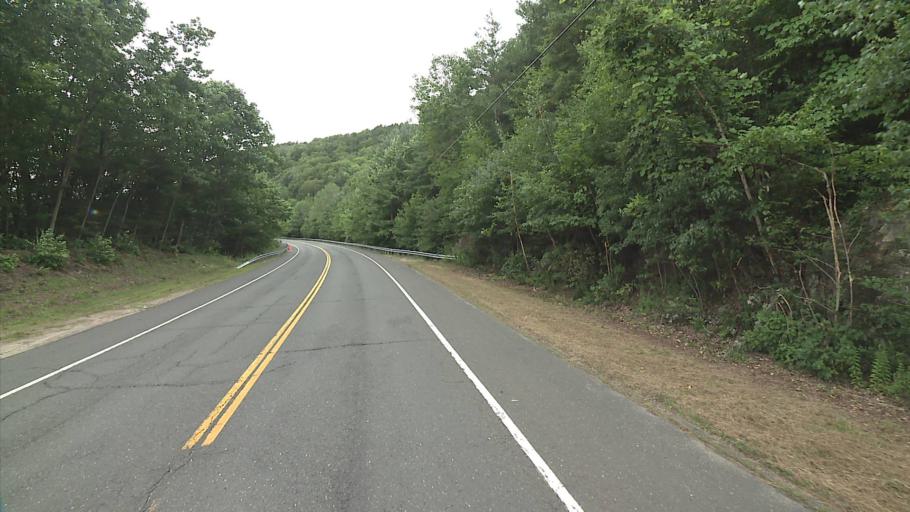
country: US
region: Connecticut
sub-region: Litchfield County
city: Winsted
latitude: 42.0190
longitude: -73.0530
